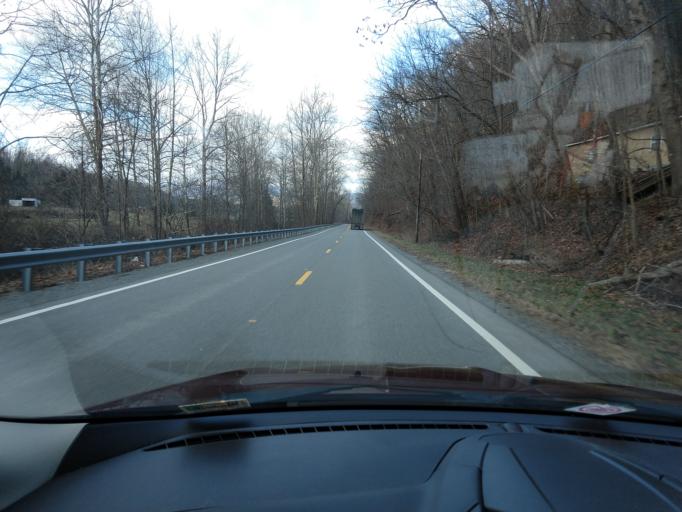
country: US
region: West Virginia
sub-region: Randolph County
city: Elkins
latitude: 38.6763
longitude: -79.9559
